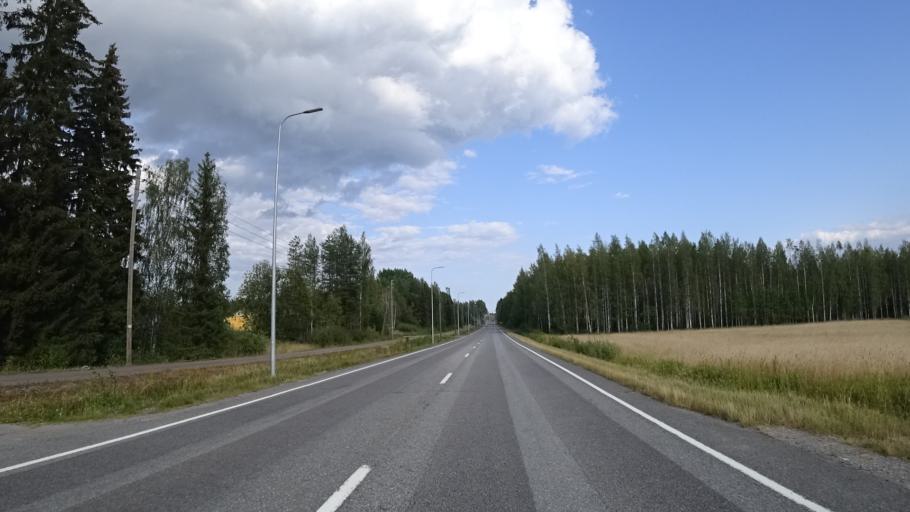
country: FI
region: South Karelia
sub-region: Imatra
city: Imatra
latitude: 61.1734
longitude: 28.7255
